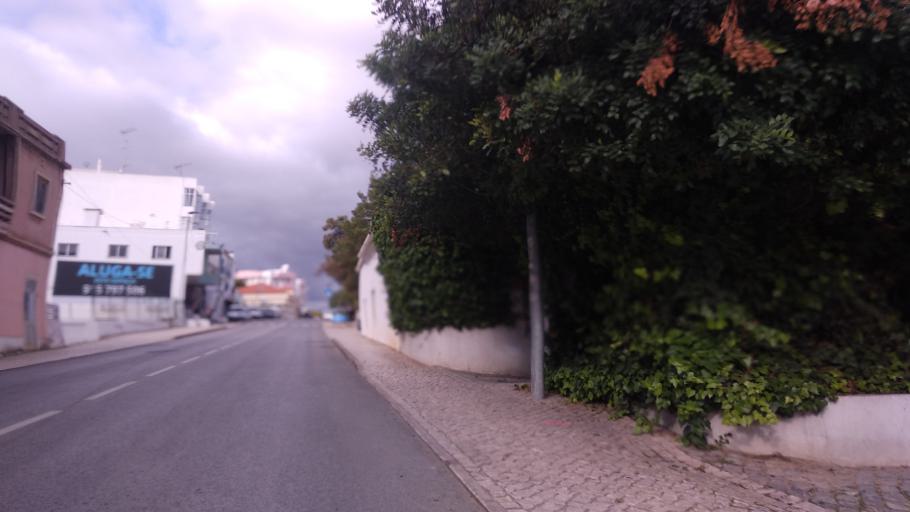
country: PT
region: Faro
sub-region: Loule
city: Almancil
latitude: 37.0879
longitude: -8.0335
